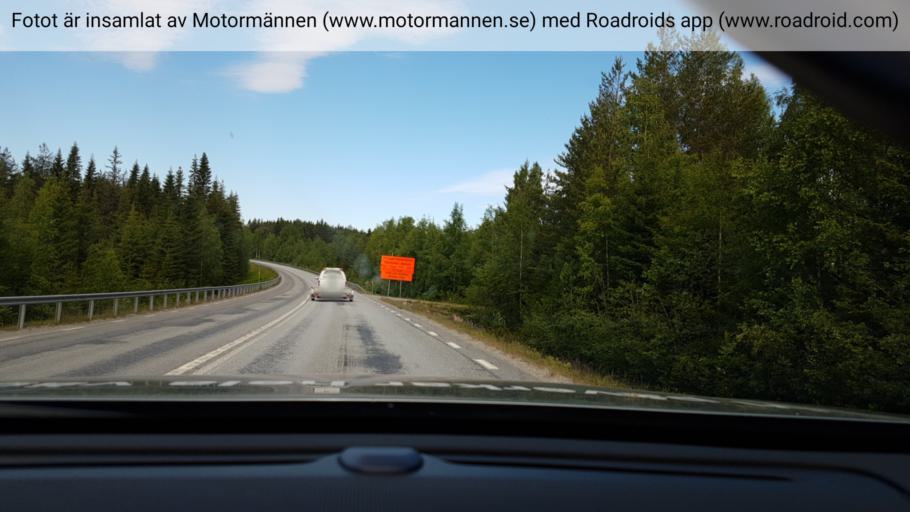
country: SE
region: Vaesterbotten
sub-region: Bjurholms Kommun
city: Bjurholm
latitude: 63.9314
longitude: 19.2581
